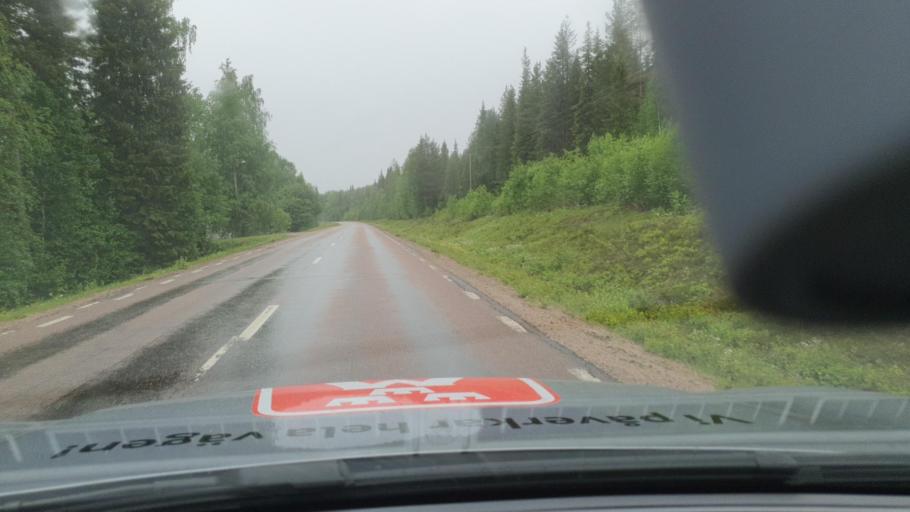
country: SE
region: Norrbotten
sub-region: Overtornea Kommun
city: OEvertornea
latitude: 66.4311
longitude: 23.3378
